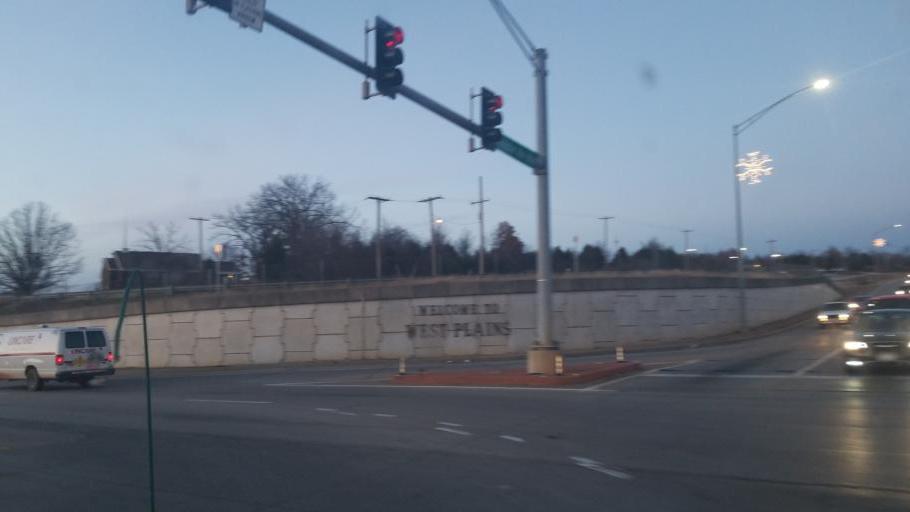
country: US
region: Missouri
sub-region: Howell County
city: West Plains
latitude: 36.7180
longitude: -91.8728
